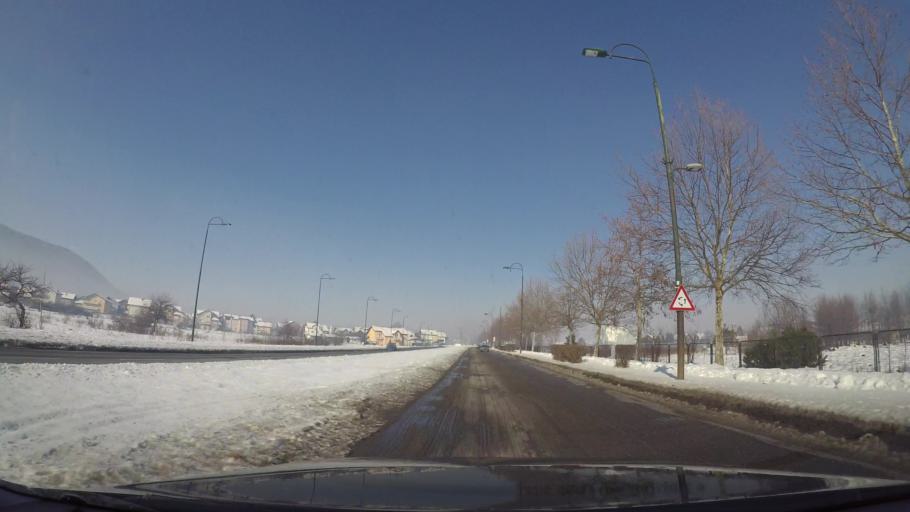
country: BA
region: Federation of Bosnia and Herzegovina
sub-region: Kanton Sarajevo
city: Sarajevo
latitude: 43.8087
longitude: 18.3108
